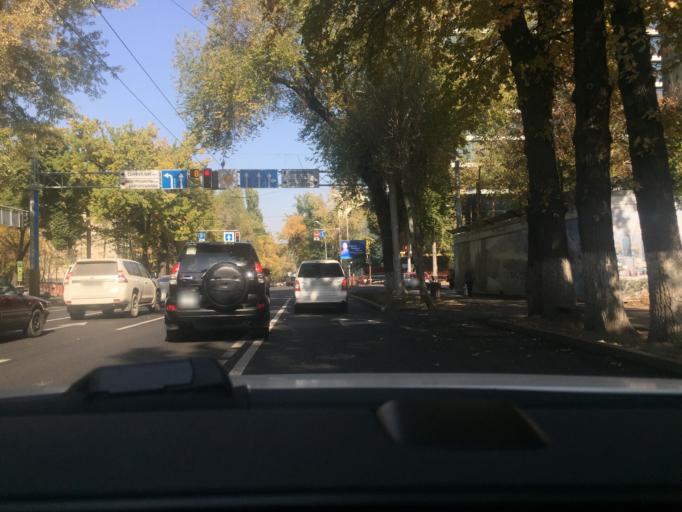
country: KZ
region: Almaty Qalasy
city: Almaty
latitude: 43.2630
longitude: 76.9387
